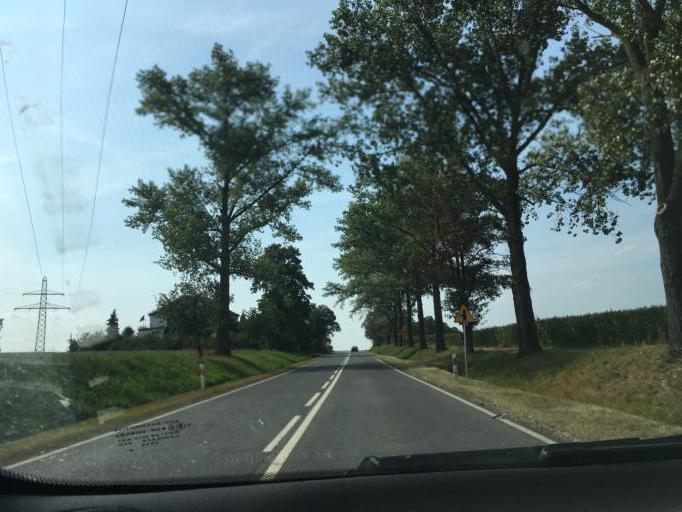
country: PL
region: Opole Voivodeship
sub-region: Powiat prudnicki
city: Laka Prudnicka
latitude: 50.4120
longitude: 17.4987
